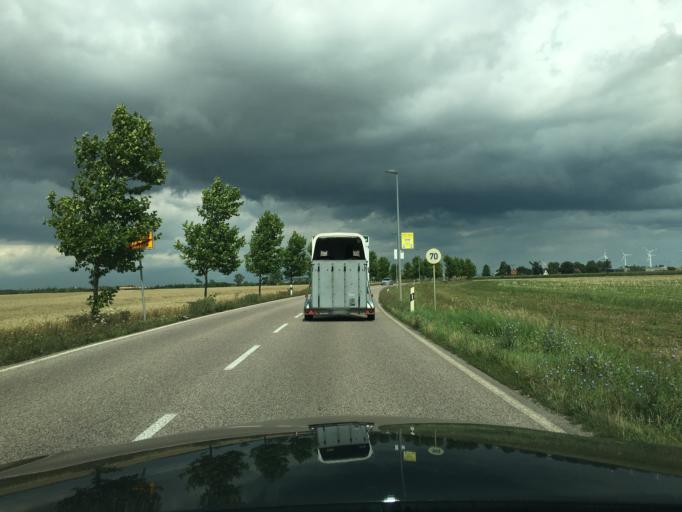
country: DE
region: Saxony-Anhalt
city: Brehna
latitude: 51.5568
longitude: 12.1964
